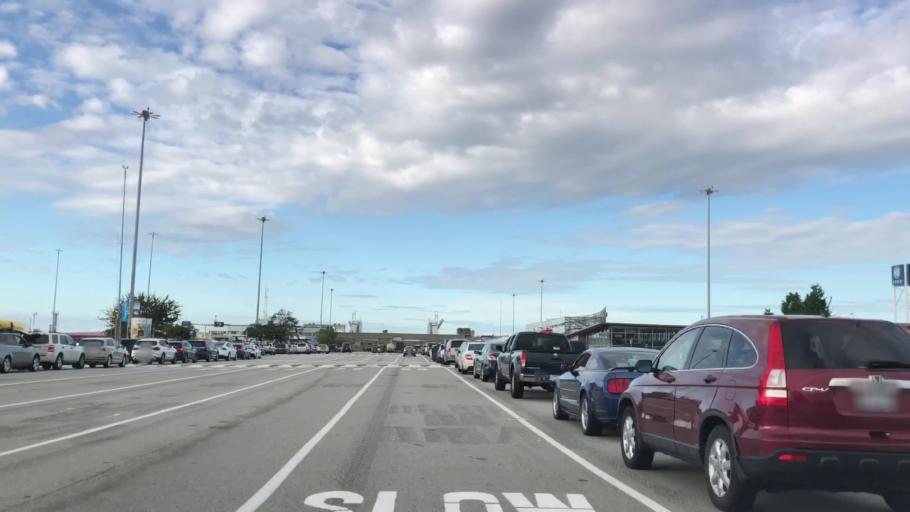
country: US
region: Washington
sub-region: Whatcom County
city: Point Roberts
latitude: 49.0094
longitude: -123.1279
